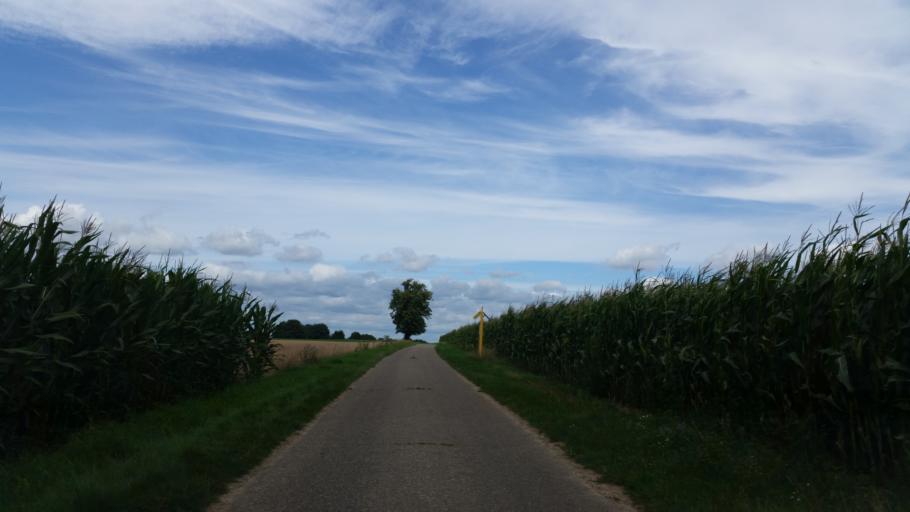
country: NL
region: Limburg
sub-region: Eijsden-Margraten
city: Margraten
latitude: 50.8359
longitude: 5.7991
